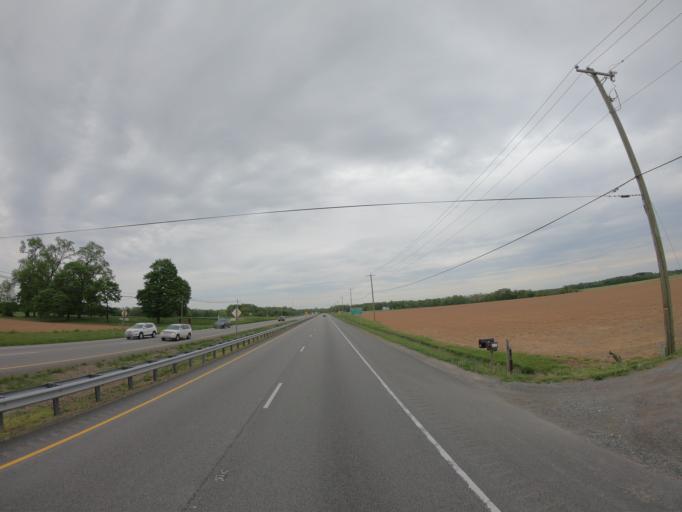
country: US
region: Maryland
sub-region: Queen Anne's County
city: Grasonville
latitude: 38.9710
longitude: -76.1218
